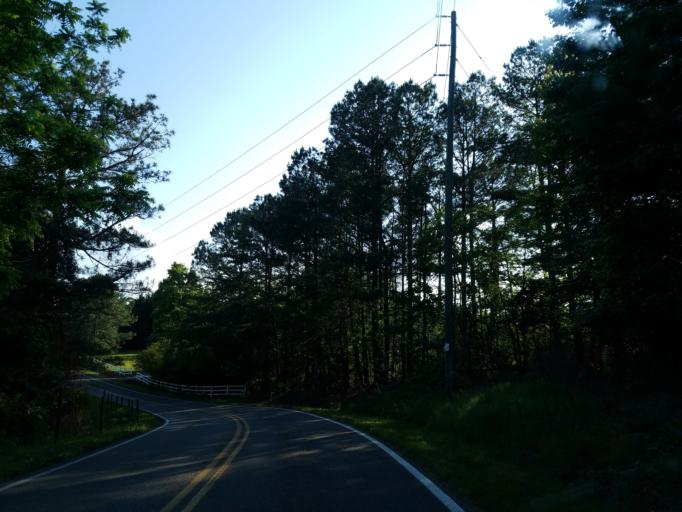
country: US
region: Georgia
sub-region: Pickens County
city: Nelson
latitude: 34.3768
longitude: -84.3234
